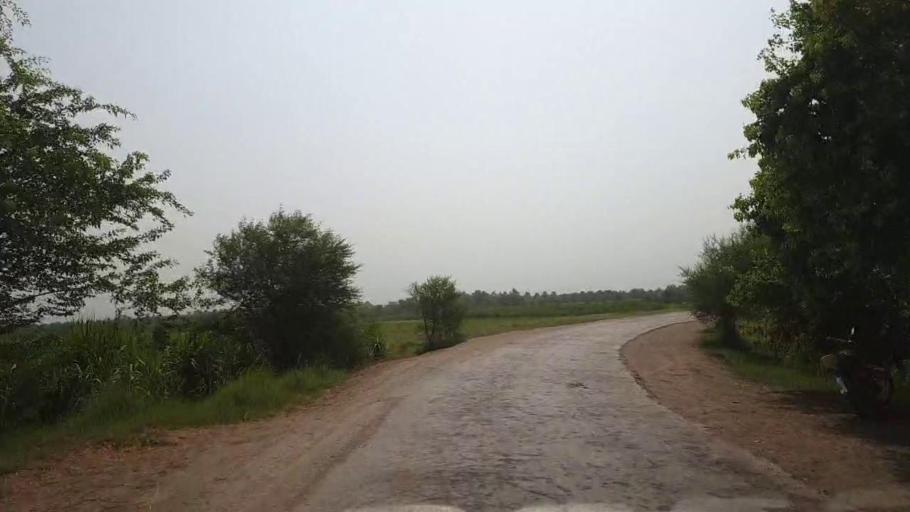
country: PK
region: Sindh
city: Gambat
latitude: 27.4325
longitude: 68.5329
